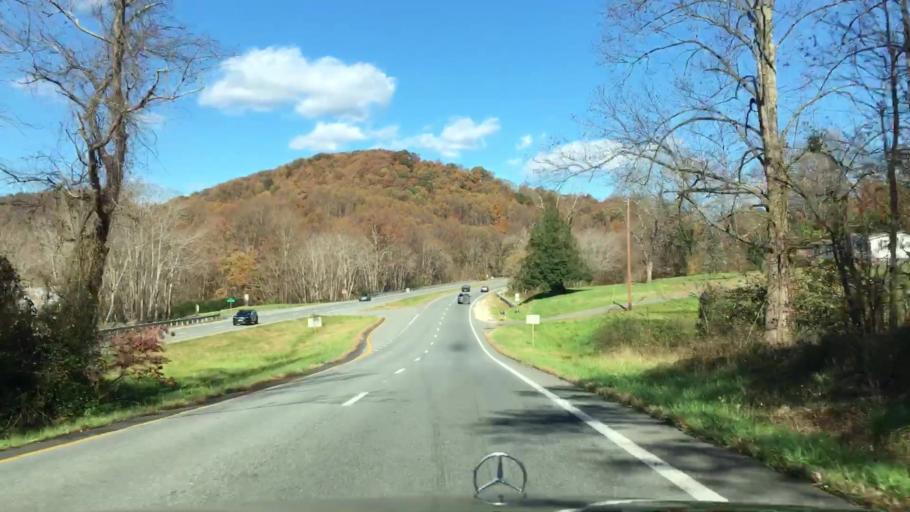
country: US
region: Virginia
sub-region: Nelson County
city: Nellysford
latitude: 37.8813
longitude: -78.7136
